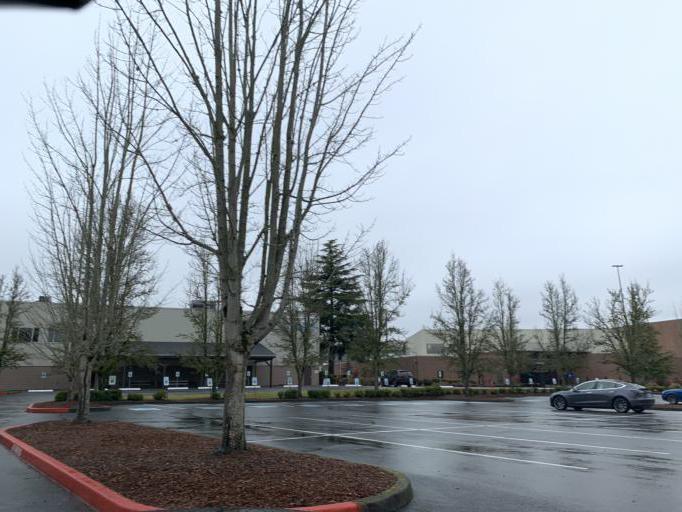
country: US
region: Washington
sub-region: Clark County
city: Walnut Grove
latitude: 45.6801
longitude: -122.5940
